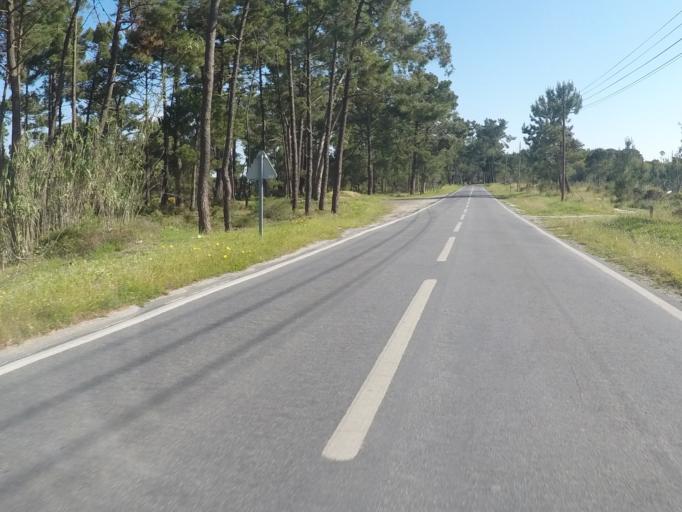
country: PT
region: Setubal
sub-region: Sesimbra
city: Sesimbra
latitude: 38.4866
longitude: -9.1583
